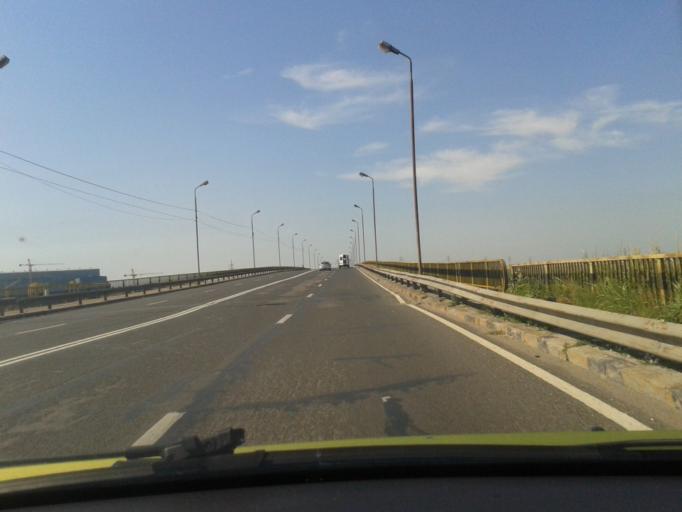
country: RO
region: Constanta
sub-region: Municipiul Mangalia
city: Mangalia
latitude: 43.8058
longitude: 28.5607
